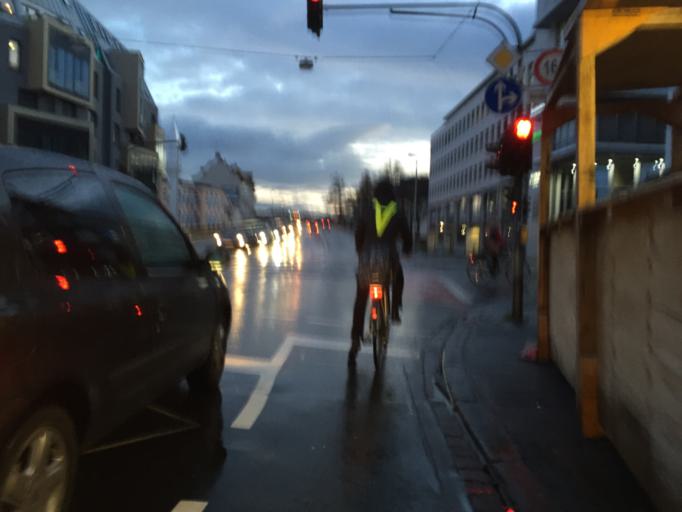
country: DE
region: North Rhine-Westphalia
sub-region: Regierungsbezirk Koln
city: Bonn
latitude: 50.7375
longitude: 7.0866
